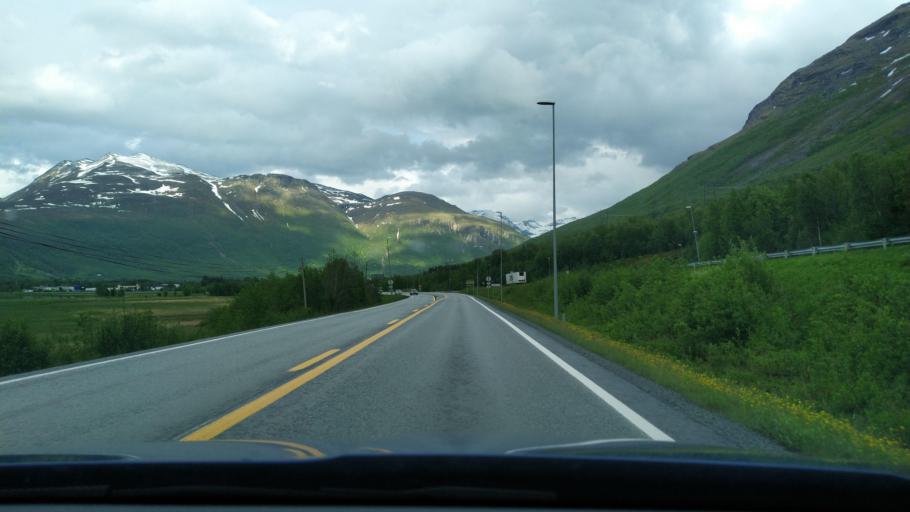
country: NO
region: Troms
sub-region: Balsfjord
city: Storsteinnes
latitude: 69.2133
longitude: 19.5299
